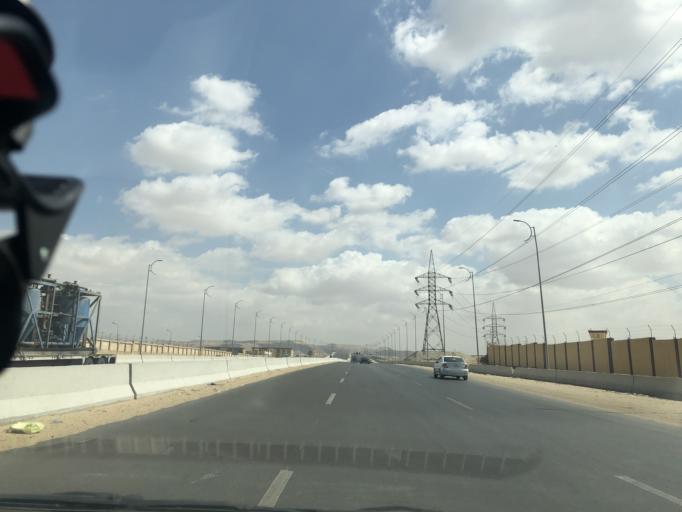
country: EG
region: Muhafazat al Qahirah
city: Halwan
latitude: 29.8701
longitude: 31.3066
